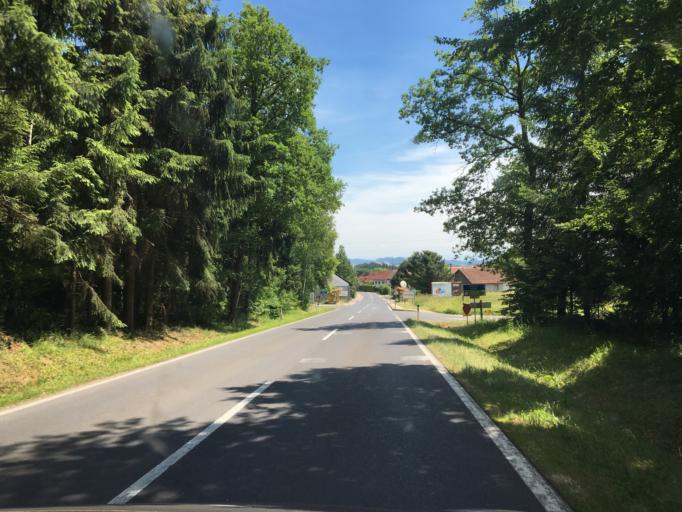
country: AT
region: Upper Austria
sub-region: Politischer Bezirk Urfahr-Umgebung
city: Engerwitzdorf
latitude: 48.3802
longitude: 14.4968
